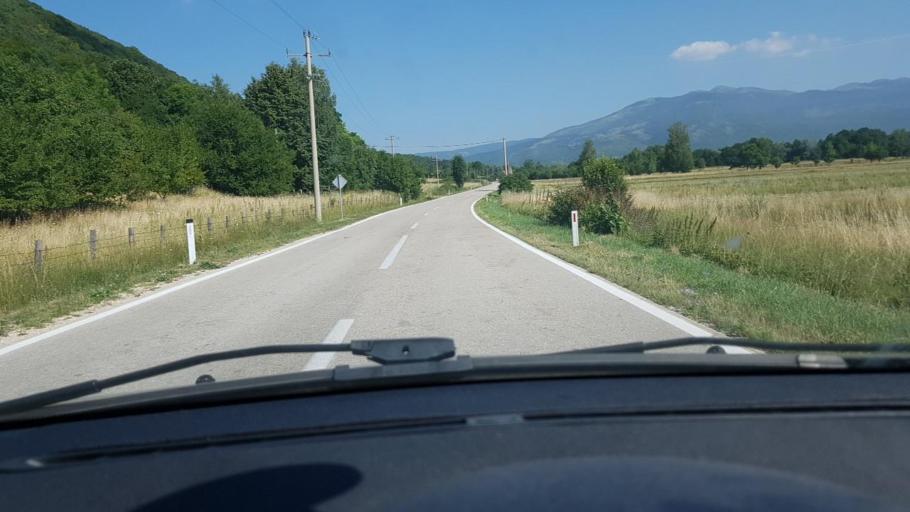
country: BA
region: Federation of Bosnia and Herzegovina
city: Glamoc
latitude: 44.0440
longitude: 16.5899
